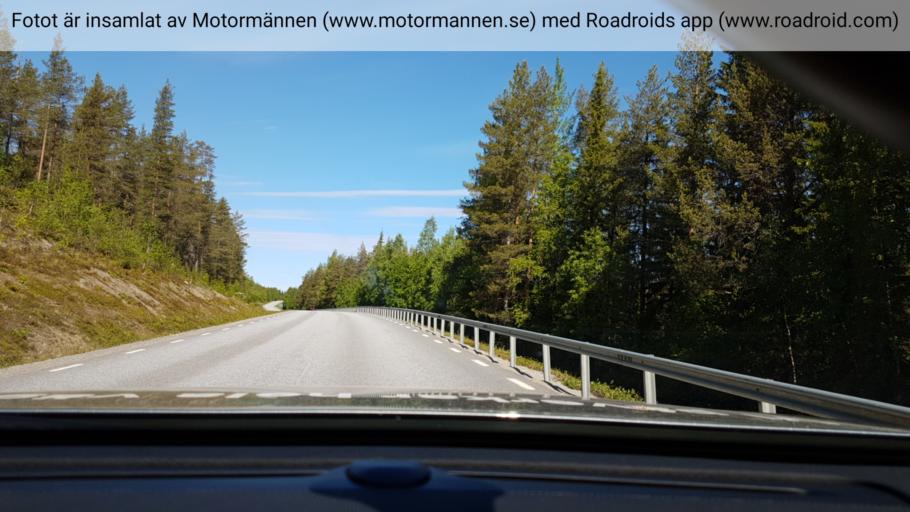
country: SE
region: Vaesterbotten
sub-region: Lycksele Kommun
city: Lycksele
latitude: 64.0301
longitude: 18.6307
